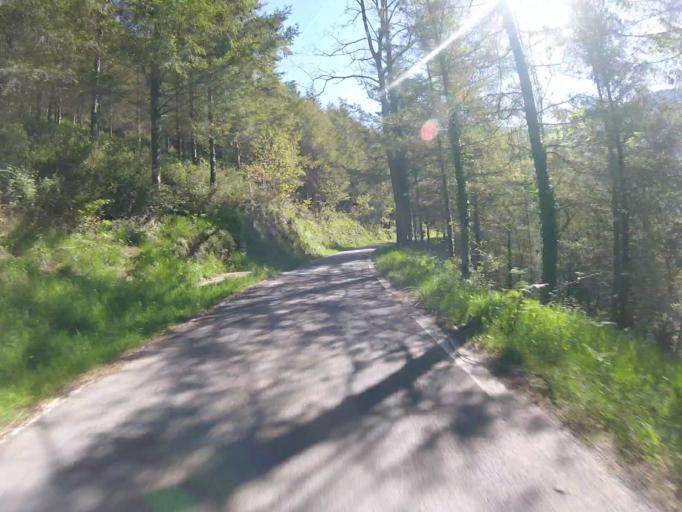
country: ES
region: Basque Country
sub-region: Provincia de Guipuzcoa
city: Errezil
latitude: 43.1912
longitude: -2.1970
